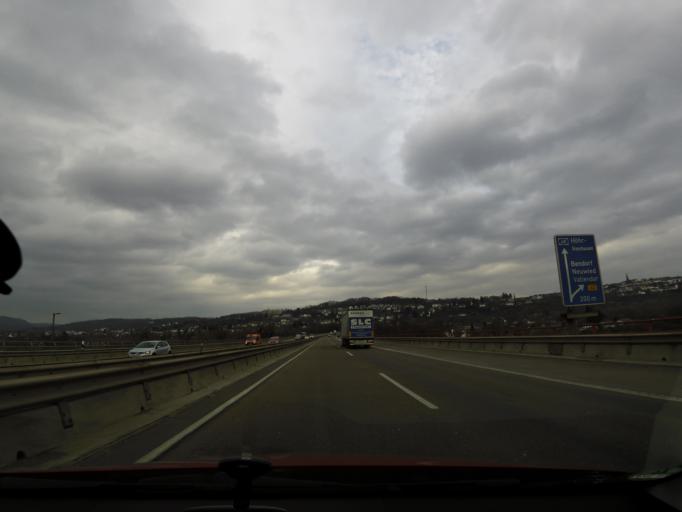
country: DE
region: Rheinland-Pfalz
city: Sankt Sebastian
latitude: 50.4109
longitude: 7.5757
